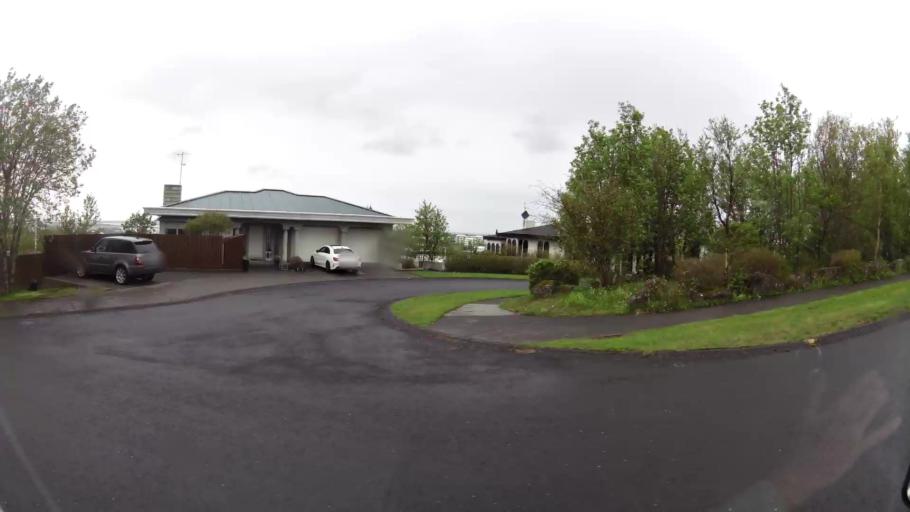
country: IS
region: Capital Region
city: Kopavogur
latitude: 64.0911
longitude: -21.8875
